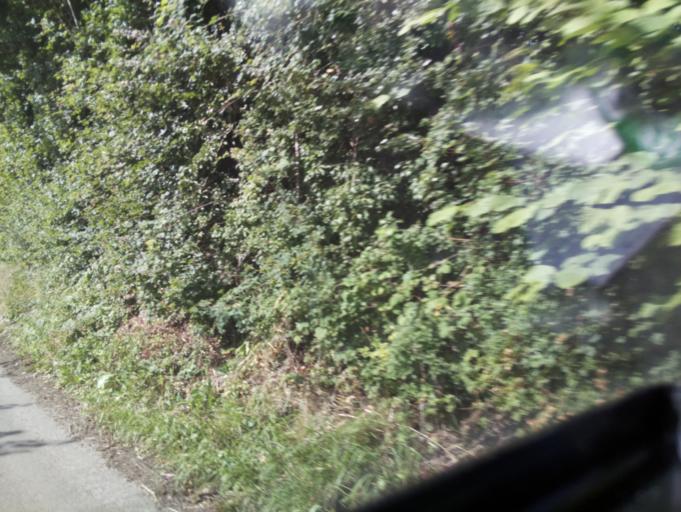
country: GB
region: England
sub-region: Wiltshire
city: Nettleton
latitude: 51.5080
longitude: -2.2616
